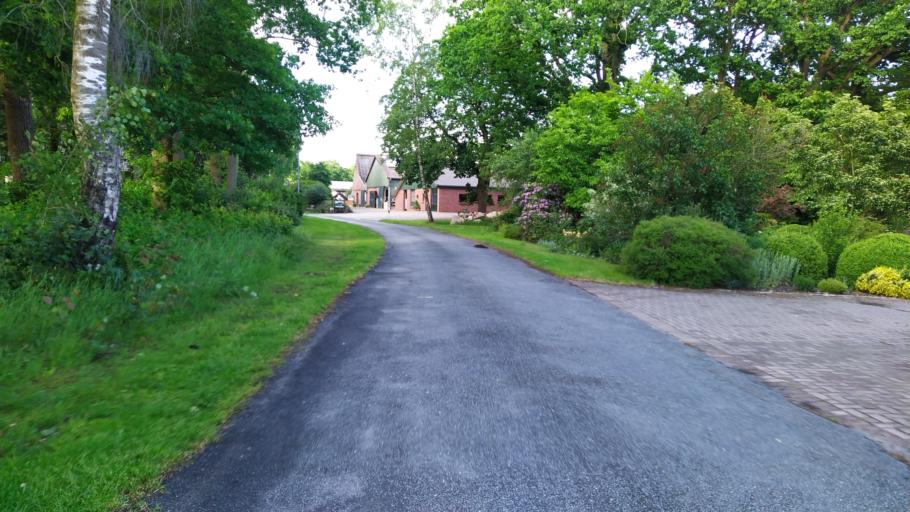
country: DE
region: Lower Saxony
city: Farven
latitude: 53.4465
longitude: 9.3193
